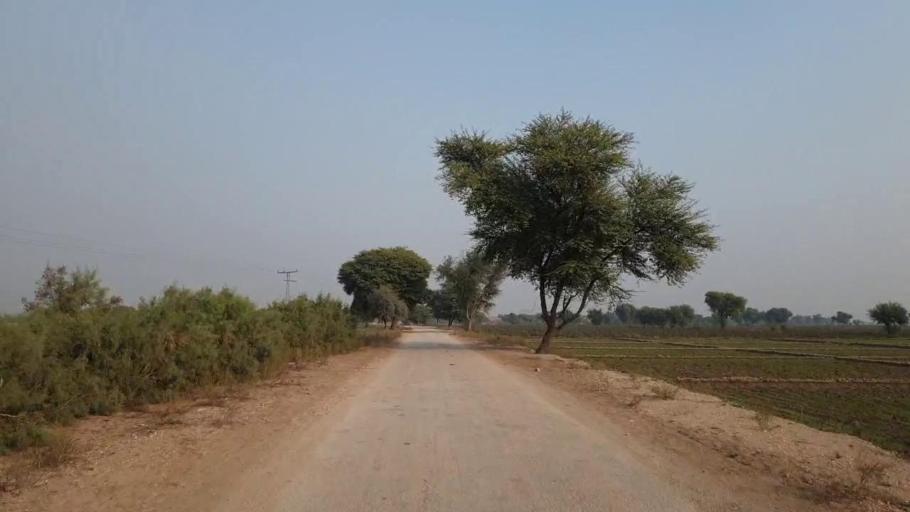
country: PK
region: Sindh
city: Bhan
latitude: 26.4960
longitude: 67.7393
